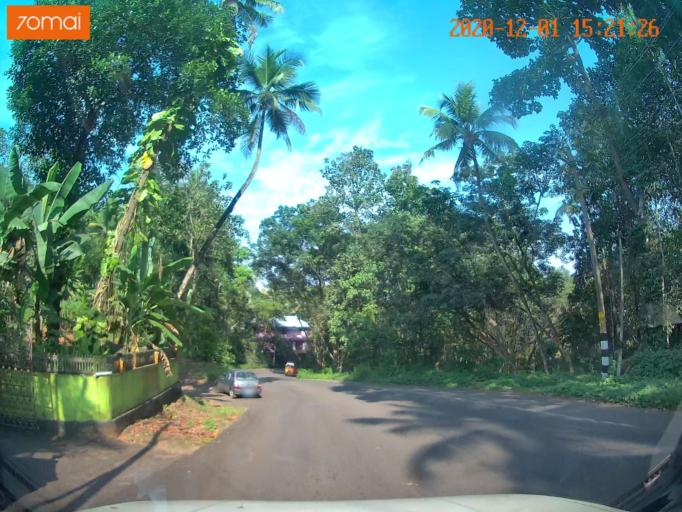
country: IN
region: Kerala
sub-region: Ernakulam
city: Ramamangalam
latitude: 9.9458
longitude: 76.5424
